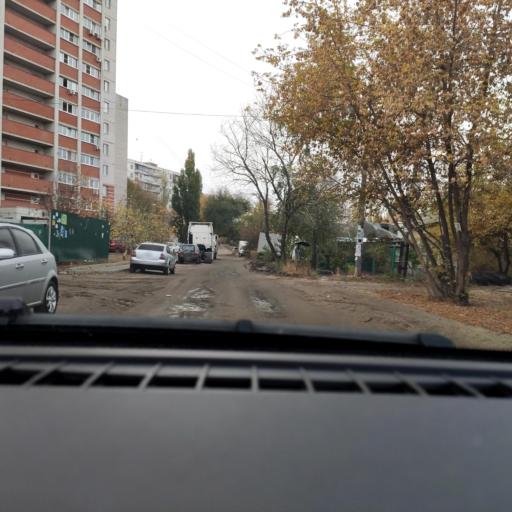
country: RU
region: Voronezj
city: Voronezh
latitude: 51.6626
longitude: 39.2837
